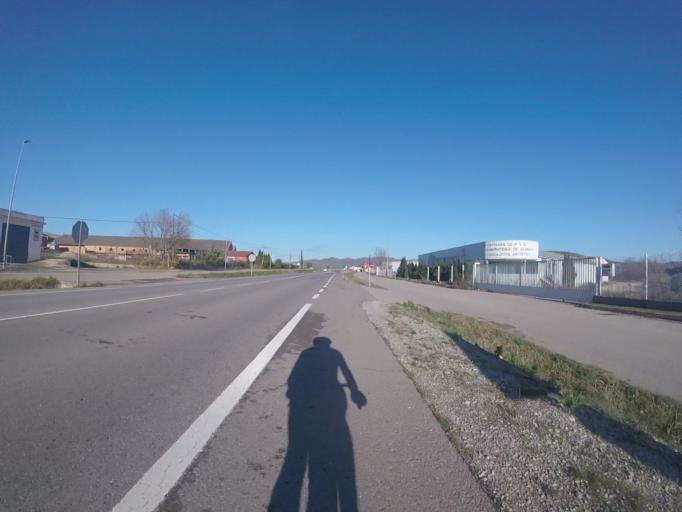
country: ES
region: Valencia
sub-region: Provincia de Castello
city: Cuevas de Vinroma
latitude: 40.3050
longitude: 0.1117
